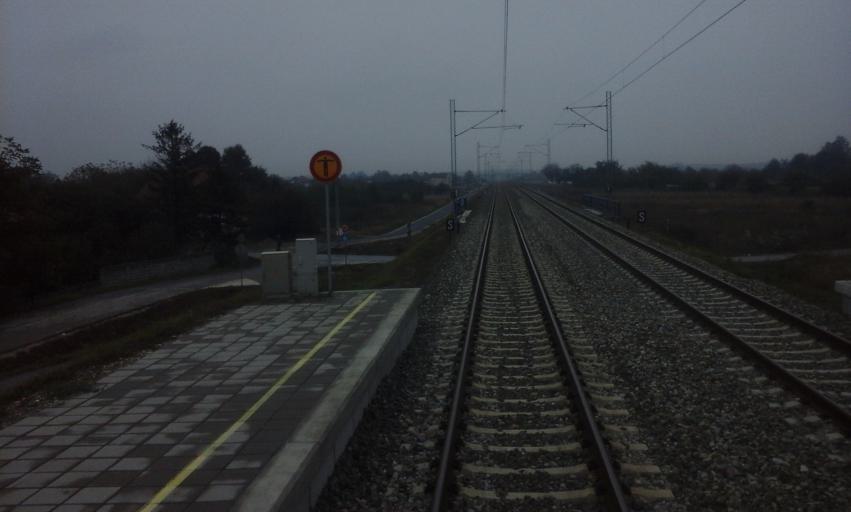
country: RS
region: Central Serbia
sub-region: Pomoravski Okrug
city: Cuprija
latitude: 43.9539
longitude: 21.3183
